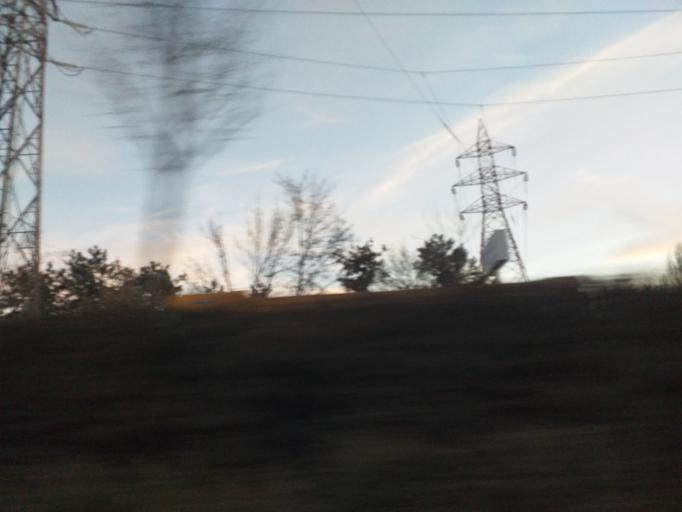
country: TR
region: Ankara
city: Ankara
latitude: 39.9549
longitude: 32.8224
